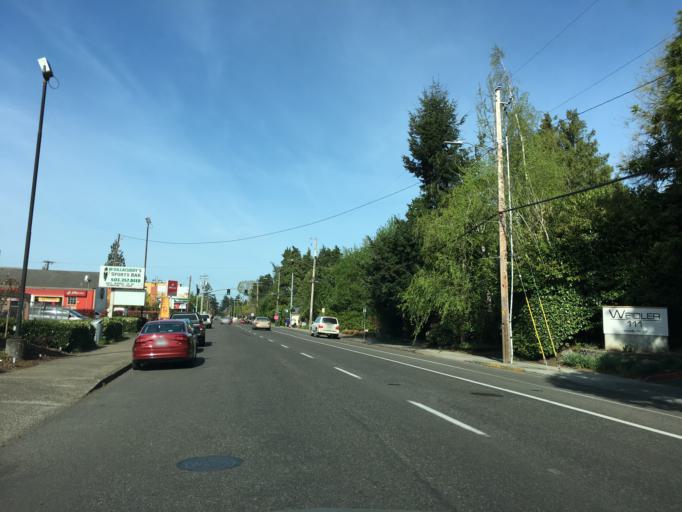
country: US
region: Oregon
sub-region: Multnomah County
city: Lents
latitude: 45.5342
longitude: -122.5478
